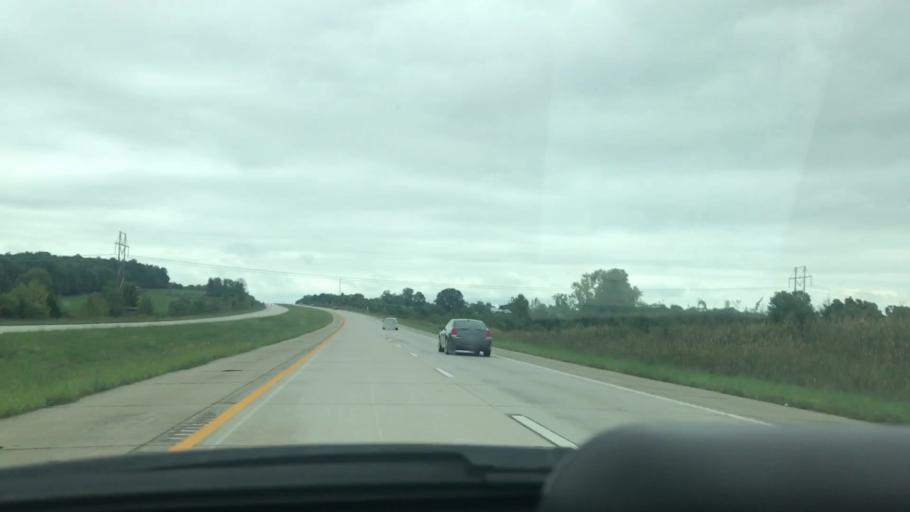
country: US
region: Missouri
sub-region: Dallas County
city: Buffalo
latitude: 37.5295
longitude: -93.1374
